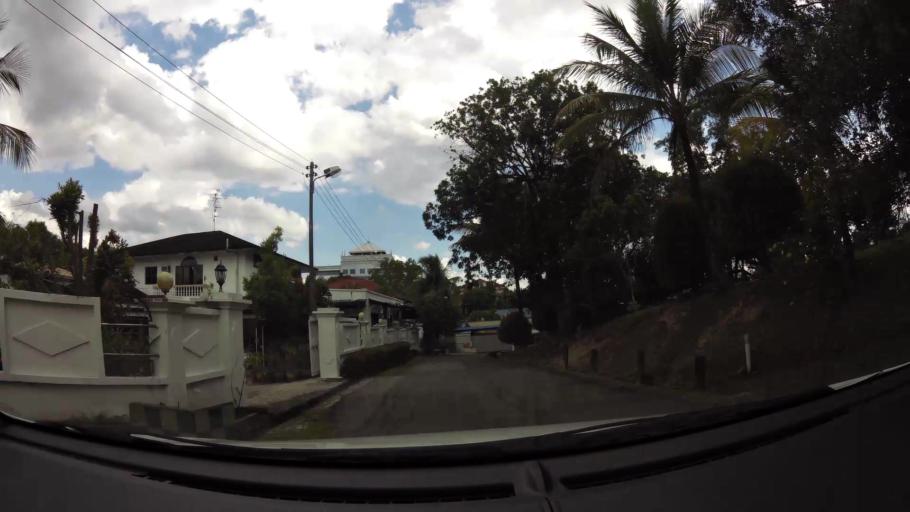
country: BN
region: Brunei and Muara
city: Bandar Seri Begawan
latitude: 4.9492
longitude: 114.9604
